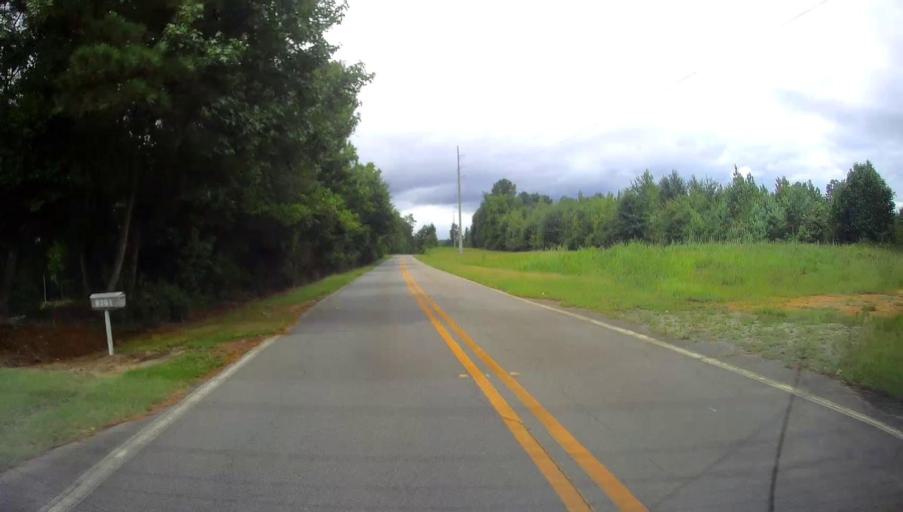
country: US
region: Georgia
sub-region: Bibb County
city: Macon
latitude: 32.7943
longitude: -83.5245
